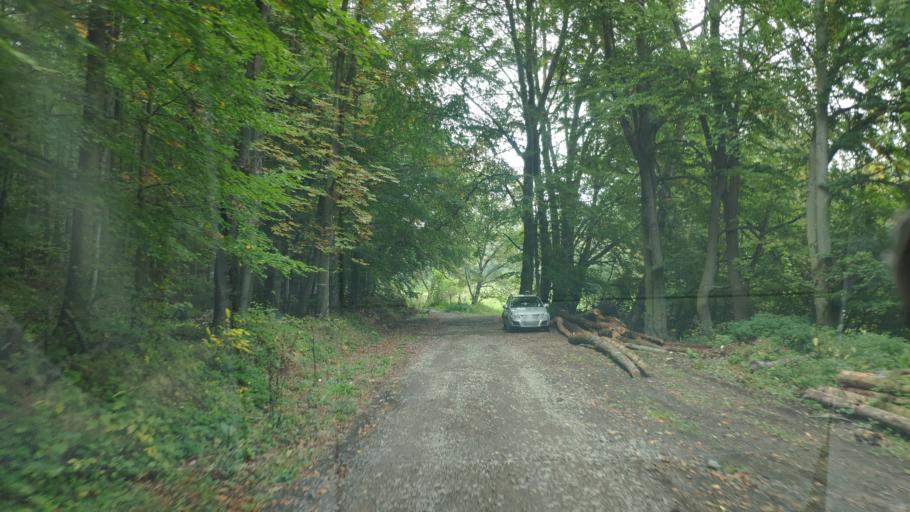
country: SK
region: Presovsky
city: Giraltovce
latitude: 48.9093
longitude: 21.4645
